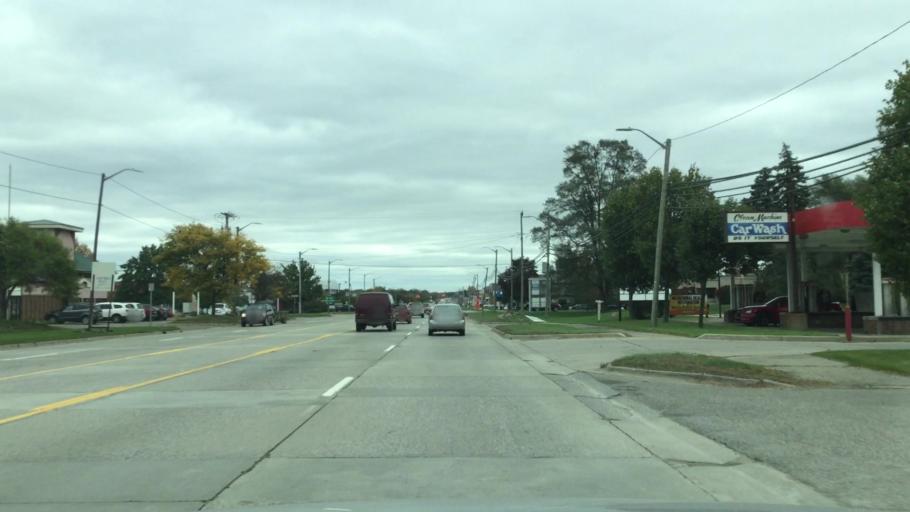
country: US
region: Michigan
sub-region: Oakland County
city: Waterford
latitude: 42.6594
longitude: -83.4220
